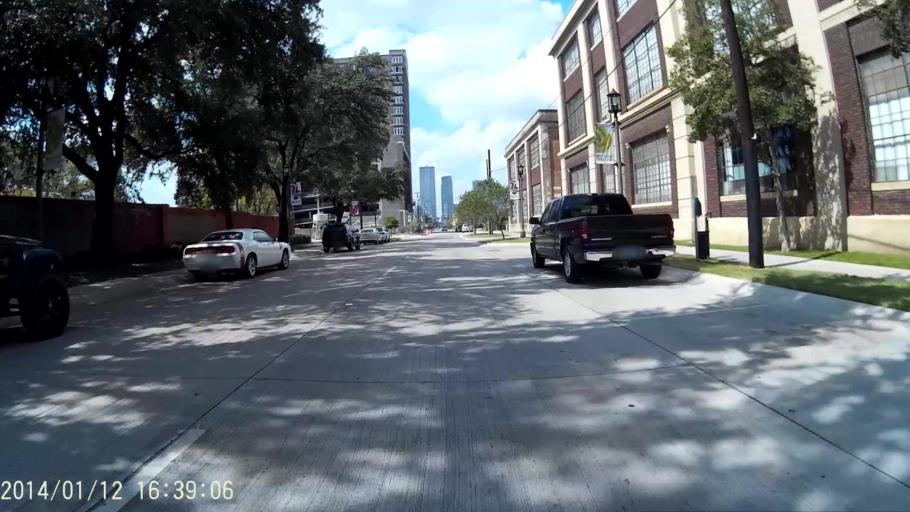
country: US
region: Texas
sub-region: Dallas County
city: Dallas
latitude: 32.7861
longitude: -96.7768
